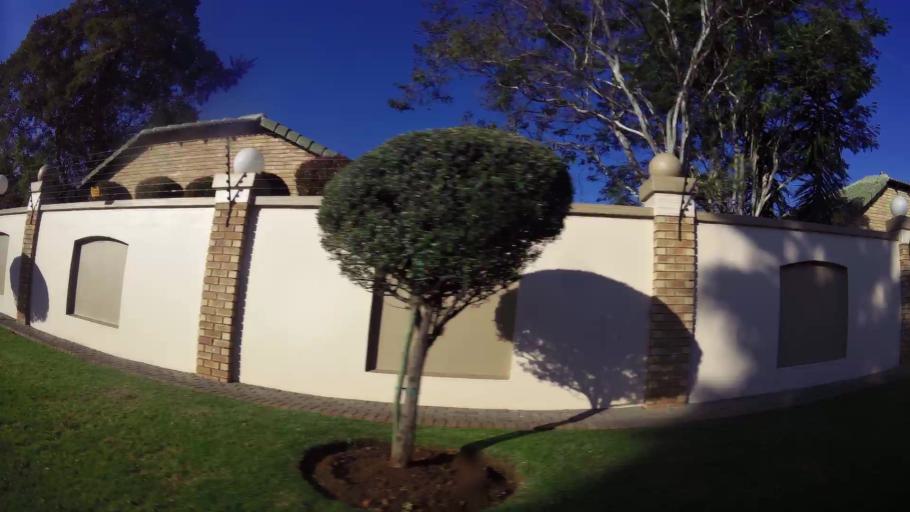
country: ZA
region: Gauteng
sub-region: City of Tshwane Metropolitan Municipality
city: Centurion
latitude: -25.8518
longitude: 28.1545
